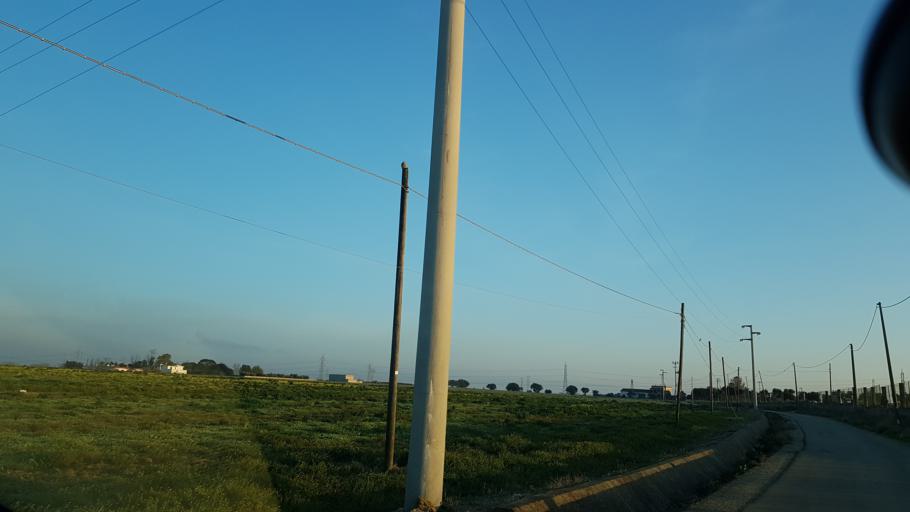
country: IT
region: Apulia
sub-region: Provincia di Brindisi
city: La Rosa
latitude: 40.6072
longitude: 17.9382
